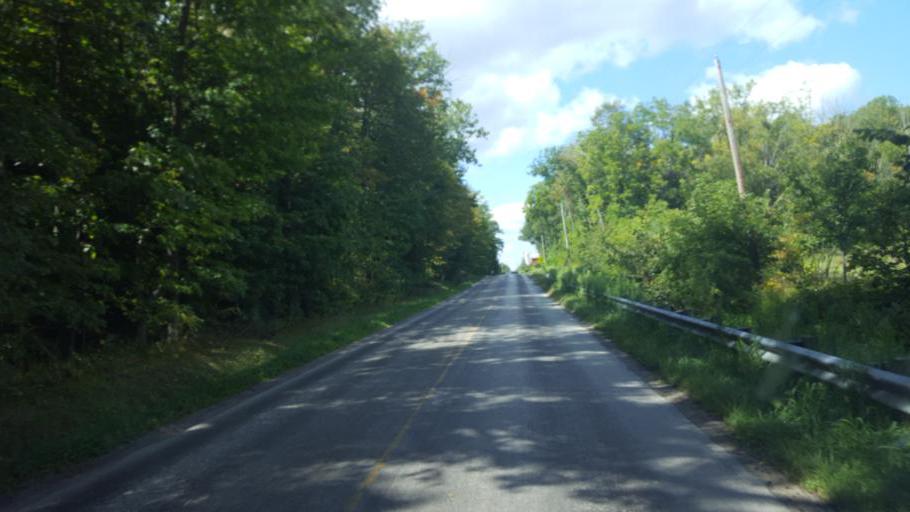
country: US
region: Ohio
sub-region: Wayne County
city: West Salem
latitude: 40.9921
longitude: -82.1698
